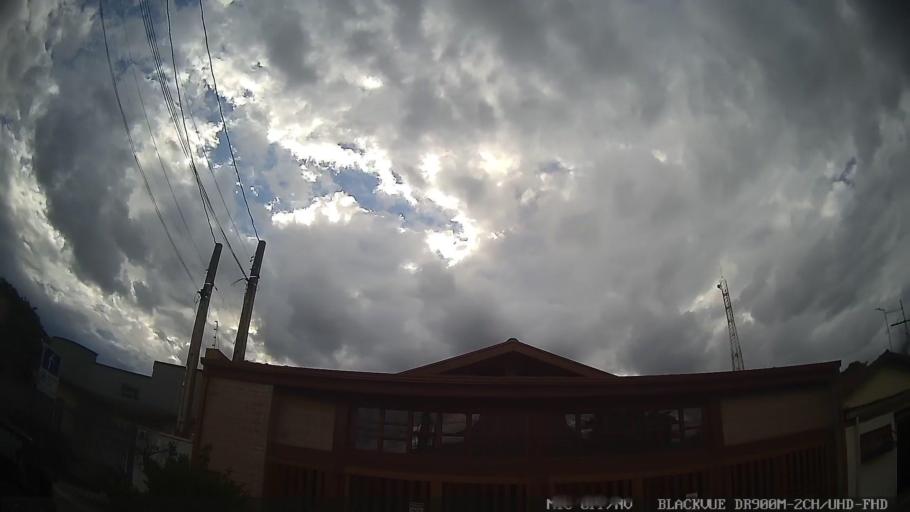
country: BR
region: Sao Paulo
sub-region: Jaguariuna
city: Jaguariuna
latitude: -22.7010
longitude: -46.9952
